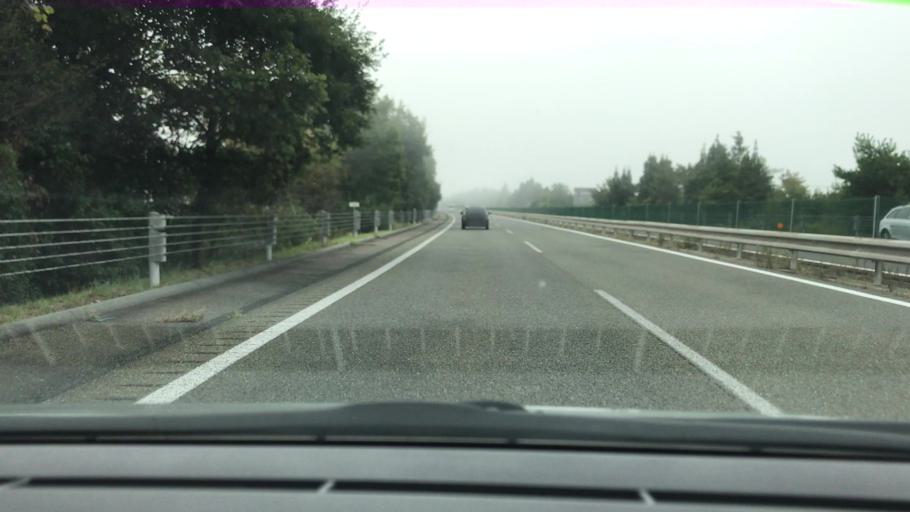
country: JP
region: Hyogo
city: Sasayama
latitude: 35.0763
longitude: 135.1703
